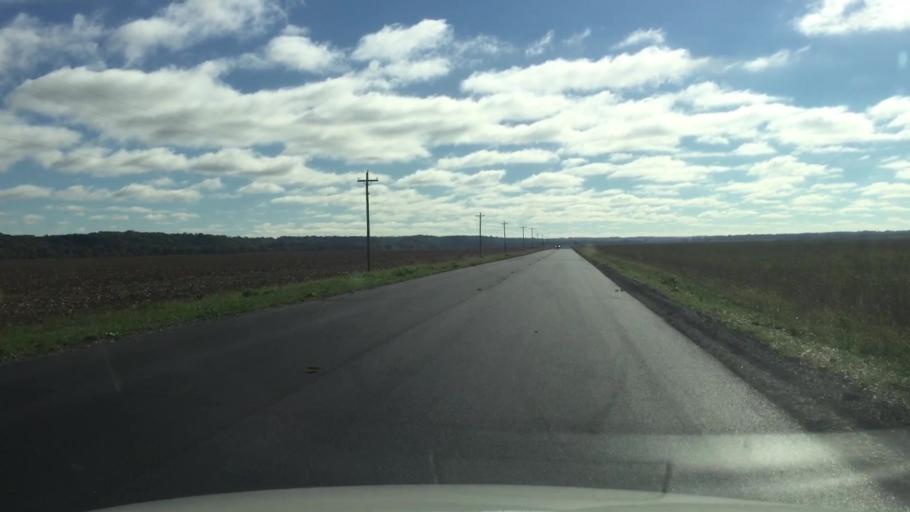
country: US
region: Missouri
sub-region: Howard County
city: New Franklin
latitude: 38.9970
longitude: -92.6676
